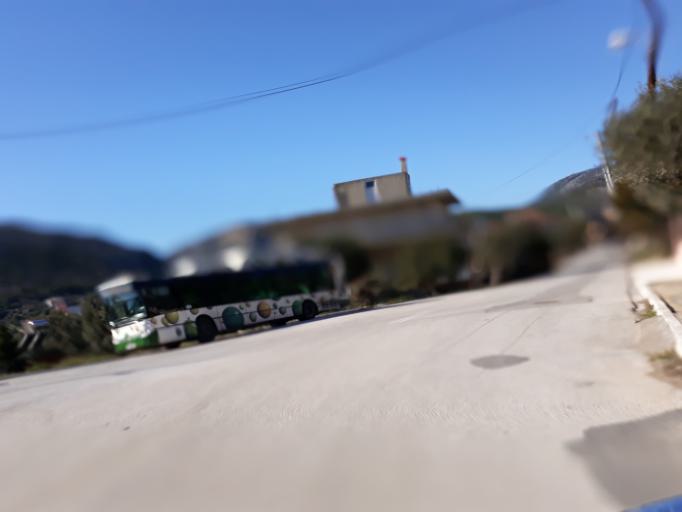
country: GR
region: Attica
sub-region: Nomarchia Dytikis Attikis
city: Fyli
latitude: 38.1079
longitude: 23.6729
